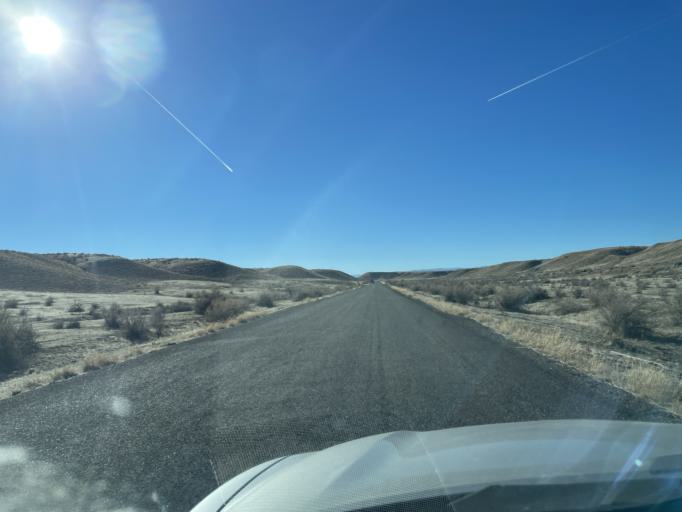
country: US
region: Colorado
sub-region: Mesa County
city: Loma
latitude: 39.2059
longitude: -109.0979
